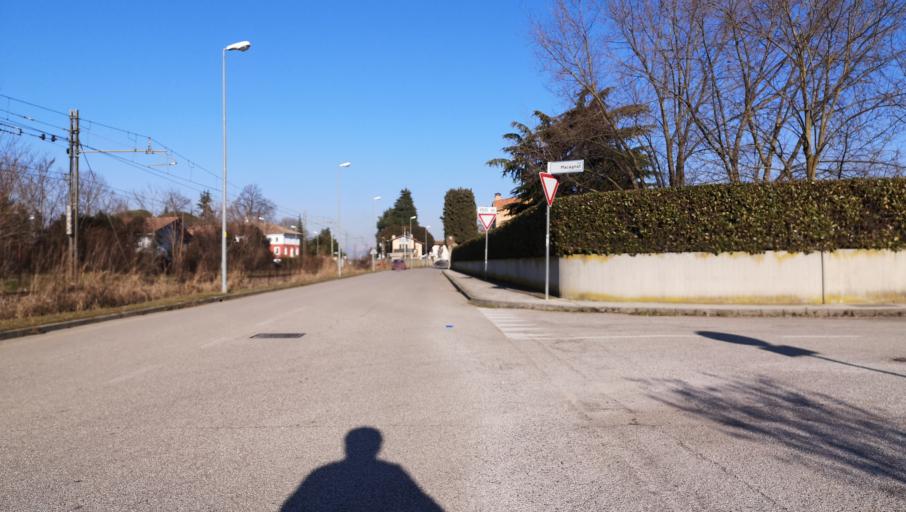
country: IT
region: Friuli Venezia Giulia
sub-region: Provincia di Udine
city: Santa Maria la Longa
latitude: 45.9316
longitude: 13.2887
